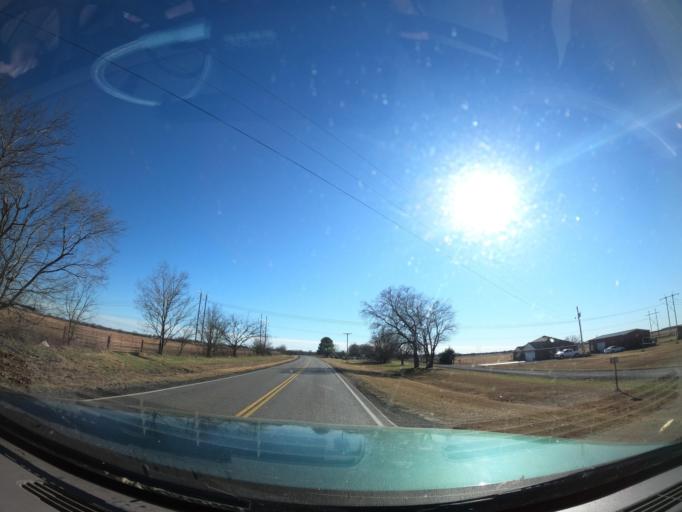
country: US
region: Oklahoma
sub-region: McIntosh County
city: Checotah
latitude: 35.5769
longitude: -95.6597
